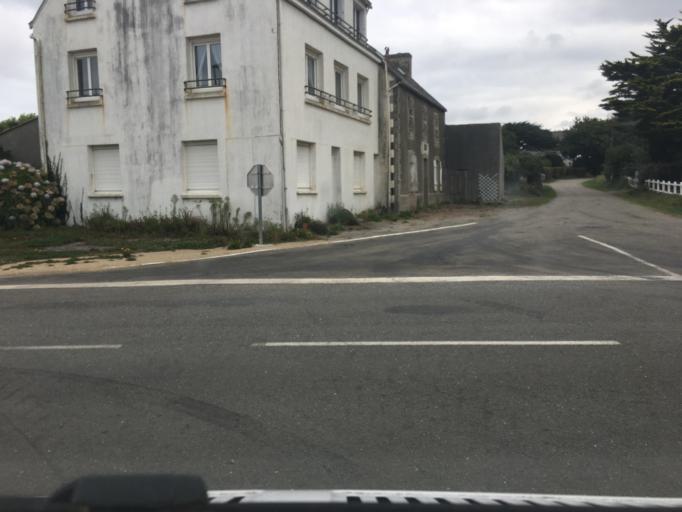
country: FR
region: Brittany
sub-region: Departement du Finistere
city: Plonevez-Porzay
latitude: 48.1320
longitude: -4.2568
